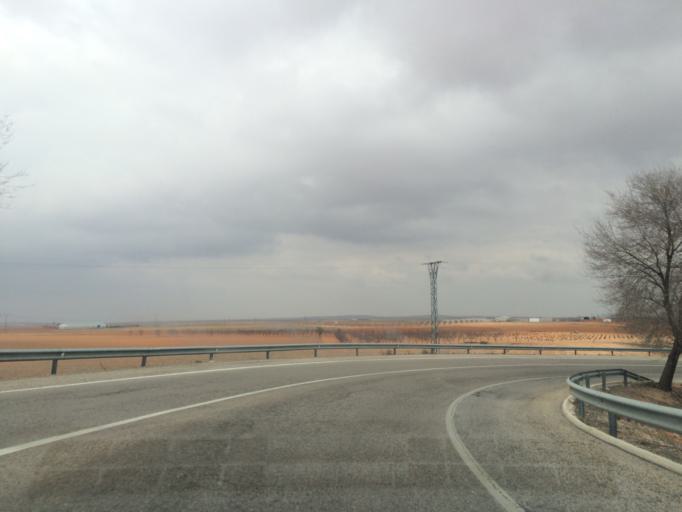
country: ES
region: Castille-La Mancha
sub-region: Province of Toledo
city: Madridejos
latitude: 39.4789
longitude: -3.5222
